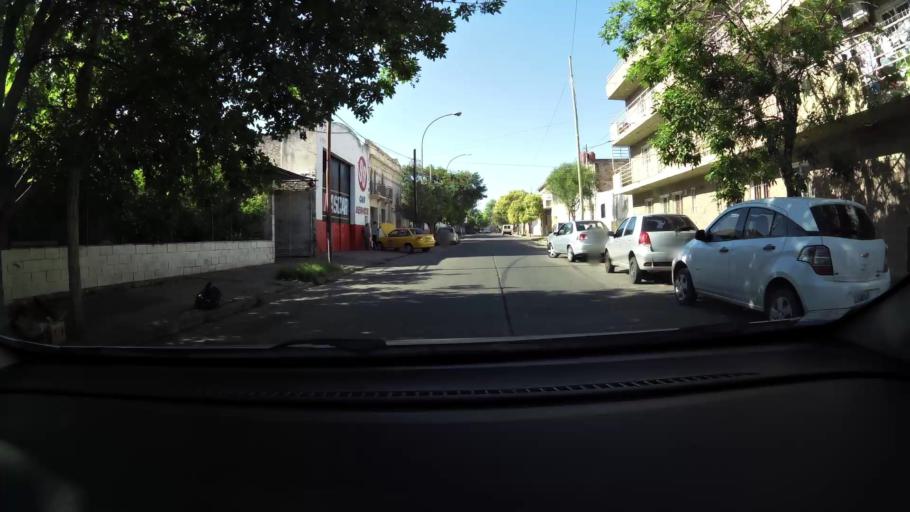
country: AR
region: Cordoba
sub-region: Departamento de Capital
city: Cordoba
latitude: -31.4244
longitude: -64.1620
